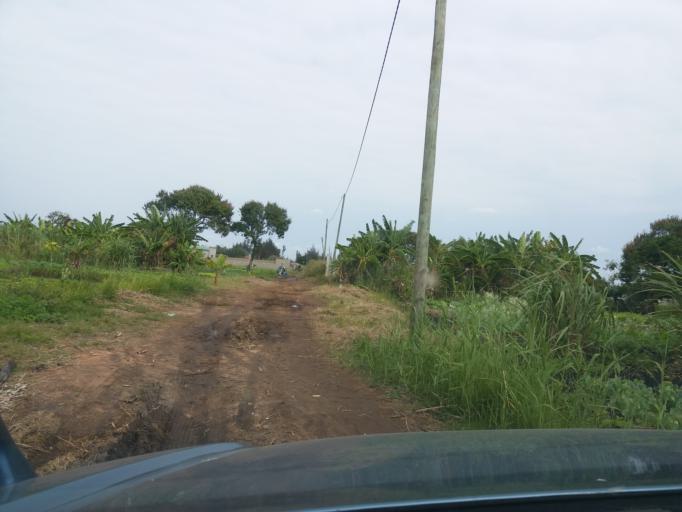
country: MZ
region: Maputo City
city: Maputo
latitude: -25.8950
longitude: 32.6356
